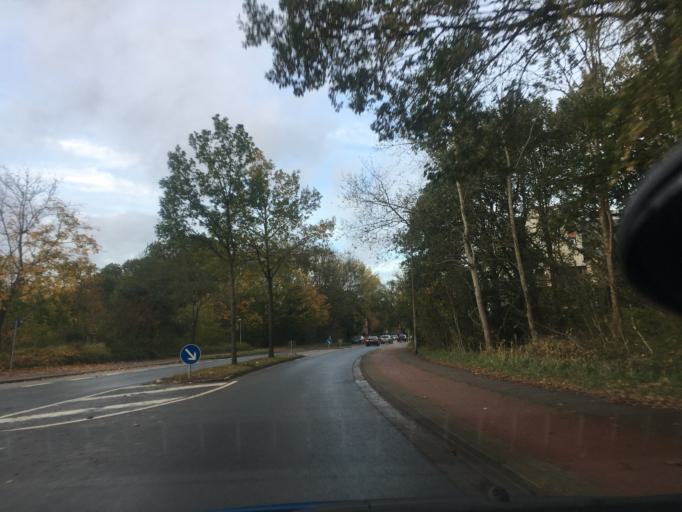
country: DE
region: Lower Saxony
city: Lueneburg
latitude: 53.2443
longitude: 10.4330
